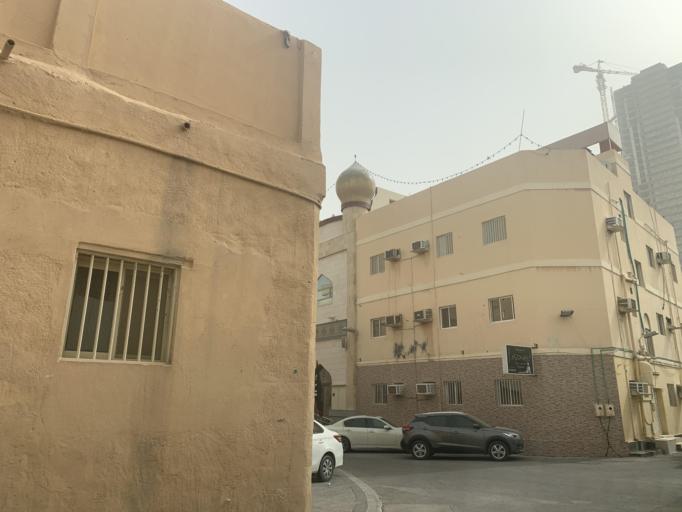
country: BH
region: Manama
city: Jidd Hafs
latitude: 26.2242
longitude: 50.5582
